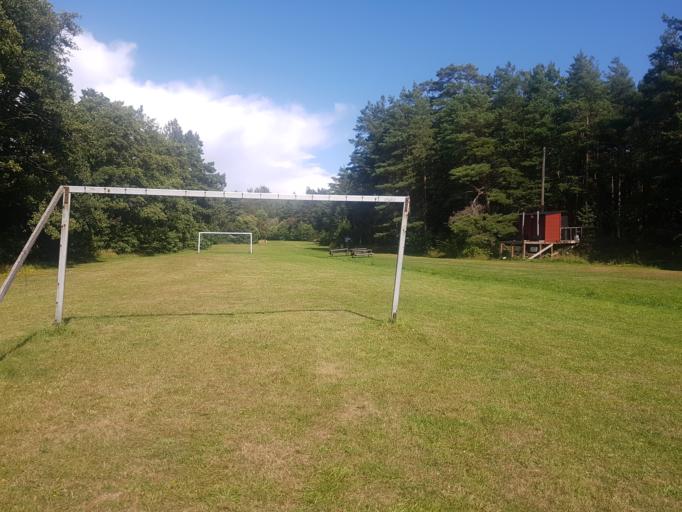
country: SE
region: Stockholm
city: Dalaro
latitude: 59.0369
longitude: 18.5148
